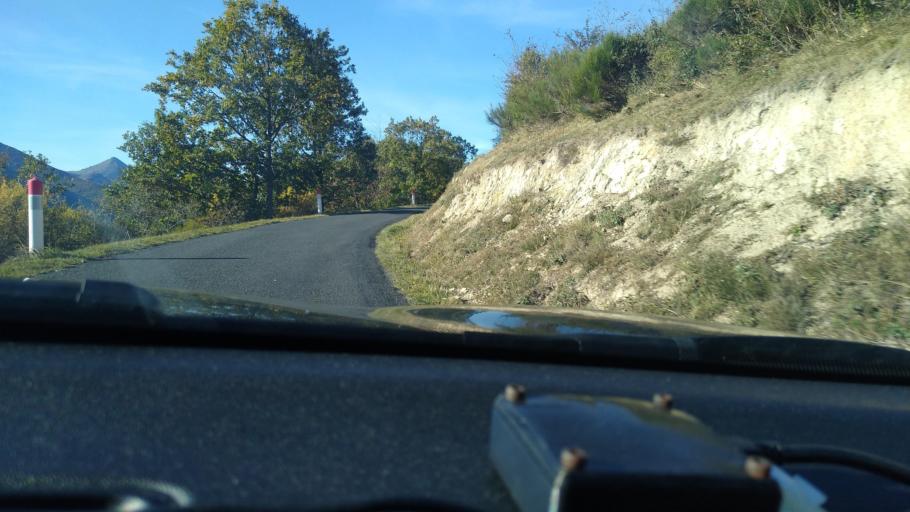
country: FR
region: Languedoc-Roussillon
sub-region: Departement de l'Aude
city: Quillan
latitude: 42.7233
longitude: 2.1222
